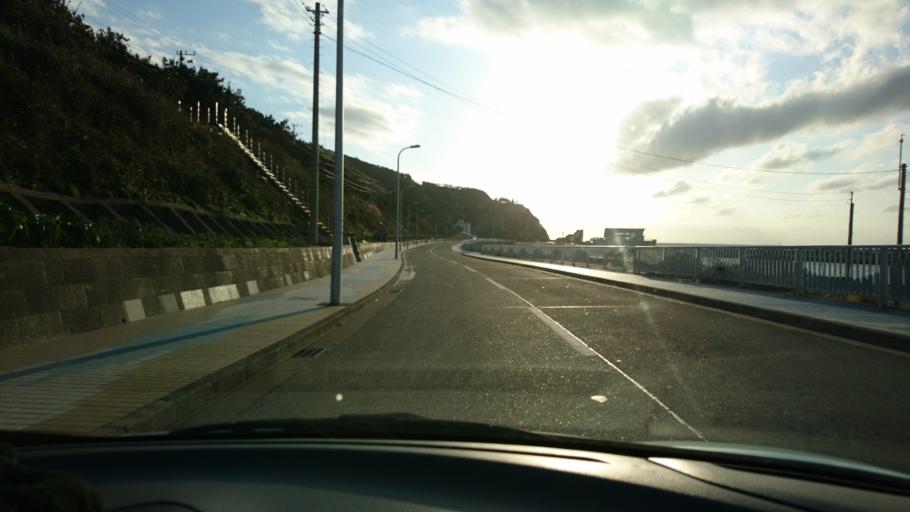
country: JP
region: Shizuoka
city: Shimoda
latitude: 34.3694
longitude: 139.2481
